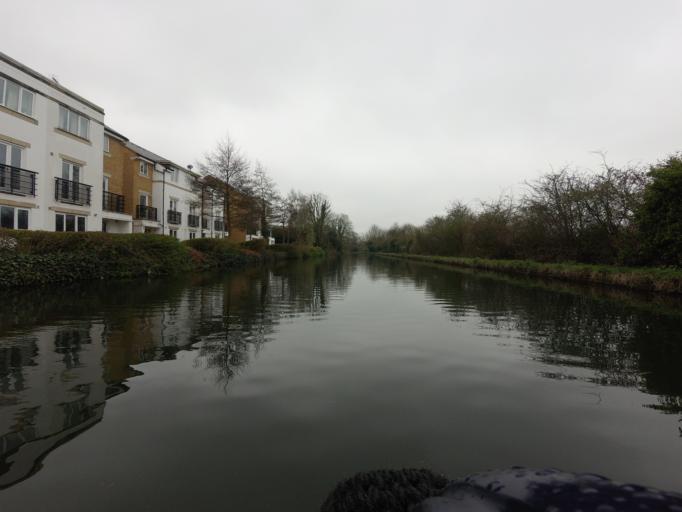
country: GB
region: England
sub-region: Hertfordshire
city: Kings Langley
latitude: 51.7110
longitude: -0.4427
